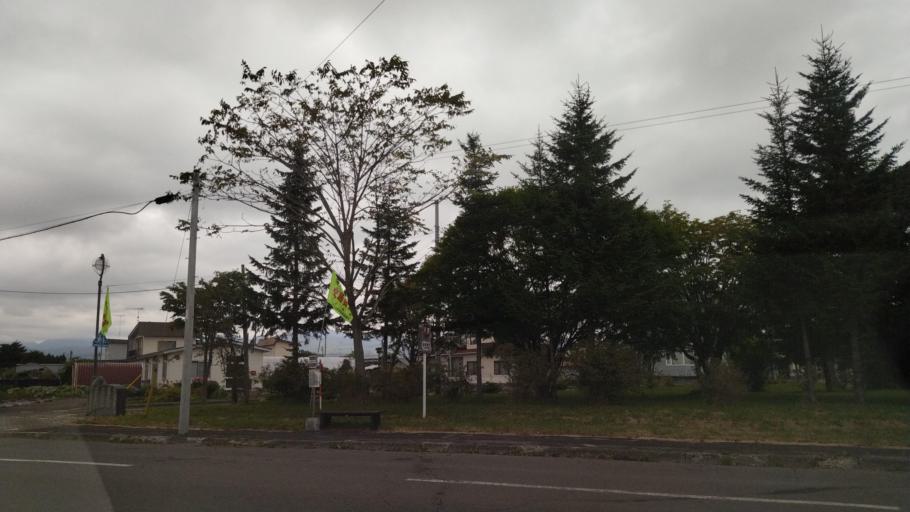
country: JP
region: Hokkaido
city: Otofuke
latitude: 43.2357
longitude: 143.2997
